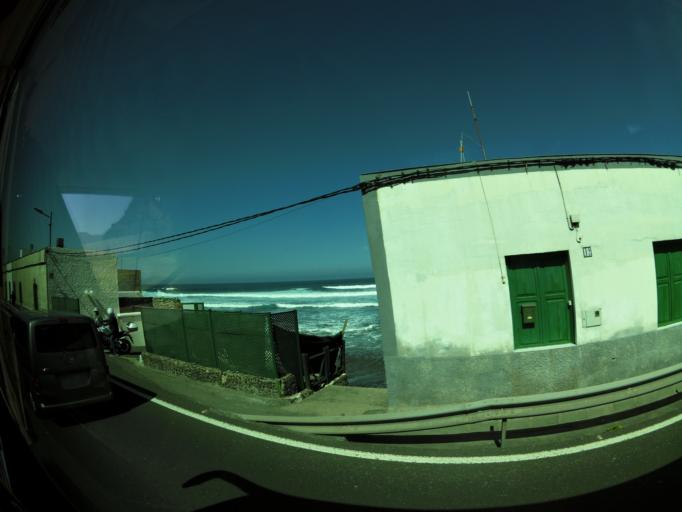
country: ES
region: Canary Islands
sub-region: Provincia de Las Palmas
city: Arucas
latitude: 28.1460
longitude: -15.5470
